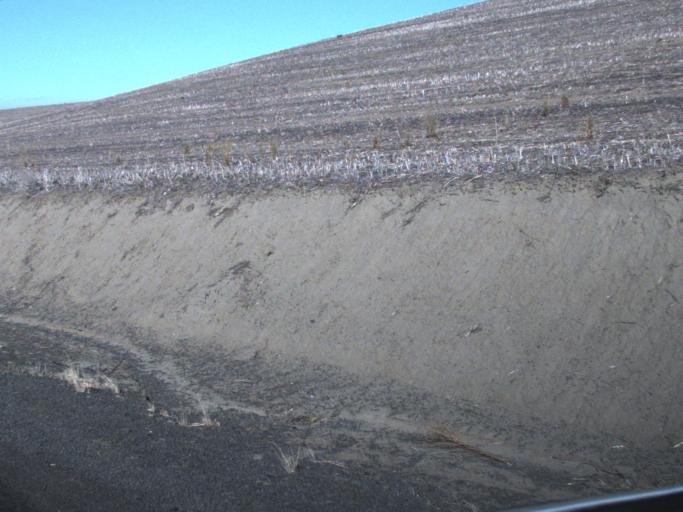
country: US
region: Washington
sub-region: Walla Walla County
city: Walla Walla
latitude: 46.1242
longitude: -118.3724
